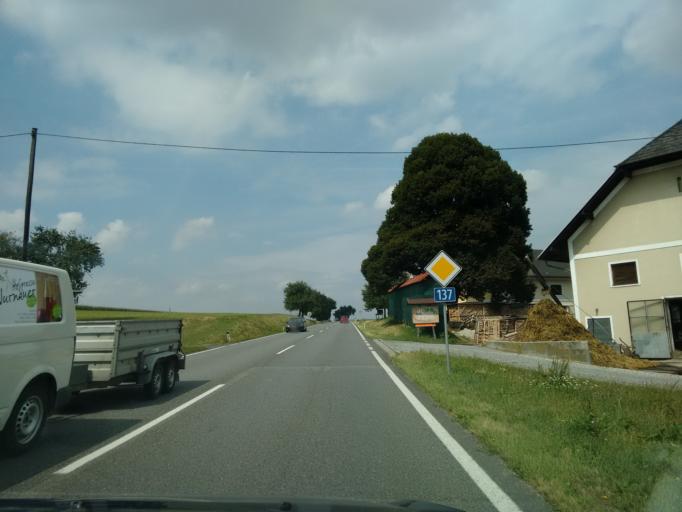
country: AT
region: Upper Austria
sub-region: Wels-Land
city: Buchkirchen
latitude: 48.2140
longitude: 13.9723
